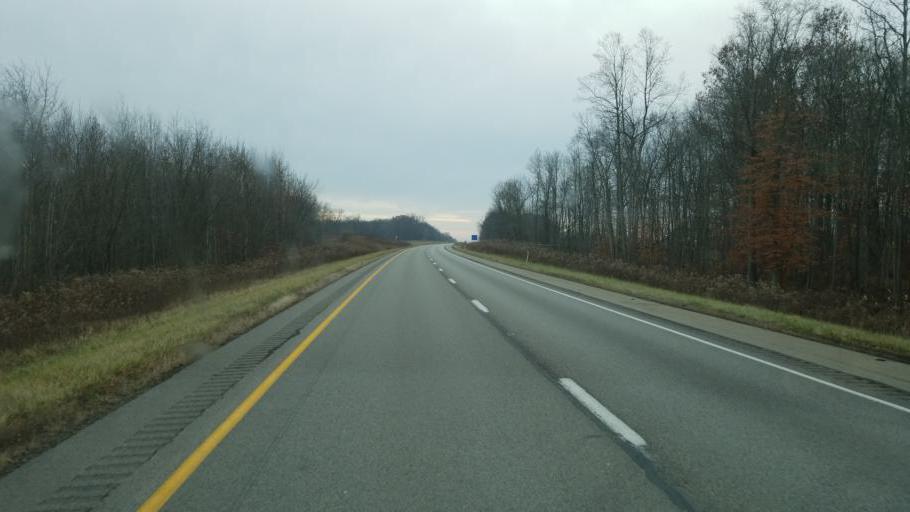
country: US
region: Pennsylvania
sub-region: Mercer County
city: Stoneboro
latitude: 41.4004
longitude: -80.1568
